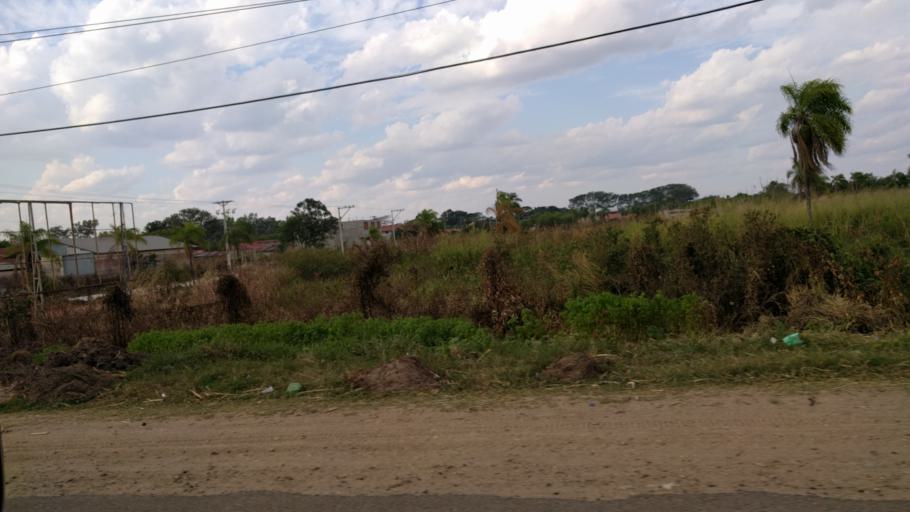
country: BO
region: Santa Cruz
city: Warnes
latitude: -17.5209
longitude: -63.1627
